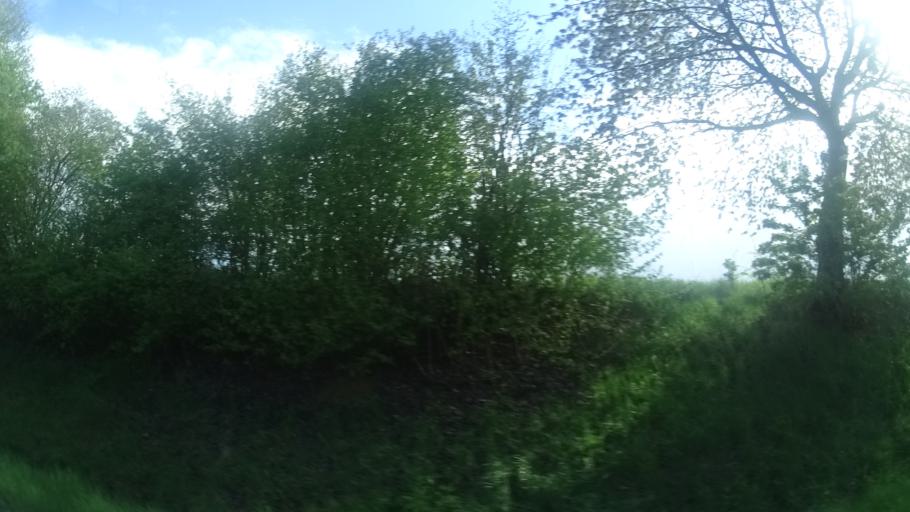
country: DE
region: Hesse
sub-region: Regierungsbezirk Giessen
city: Langgons
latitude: 50.5014
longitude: 8.6544
